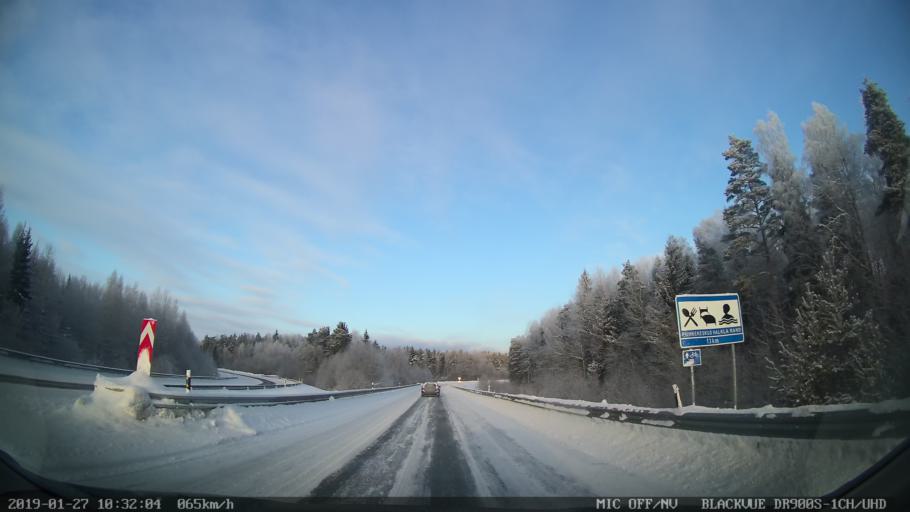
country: EE
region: Harju
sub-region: Raasiku vald
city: Raasiku
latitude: 59.4376
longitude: 25.1889
